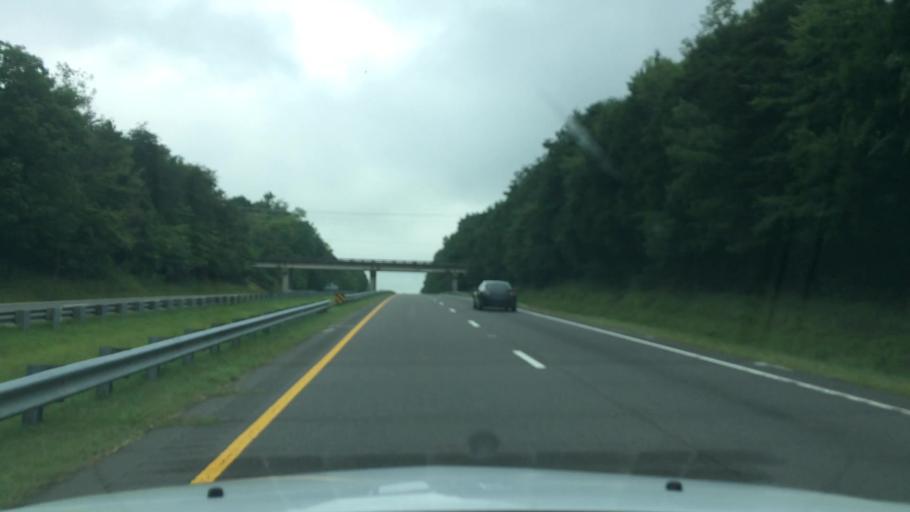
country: US
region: North Carolina
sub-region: Forsyth County
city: Lewisville
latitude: 36.1017
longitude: -80.4873
